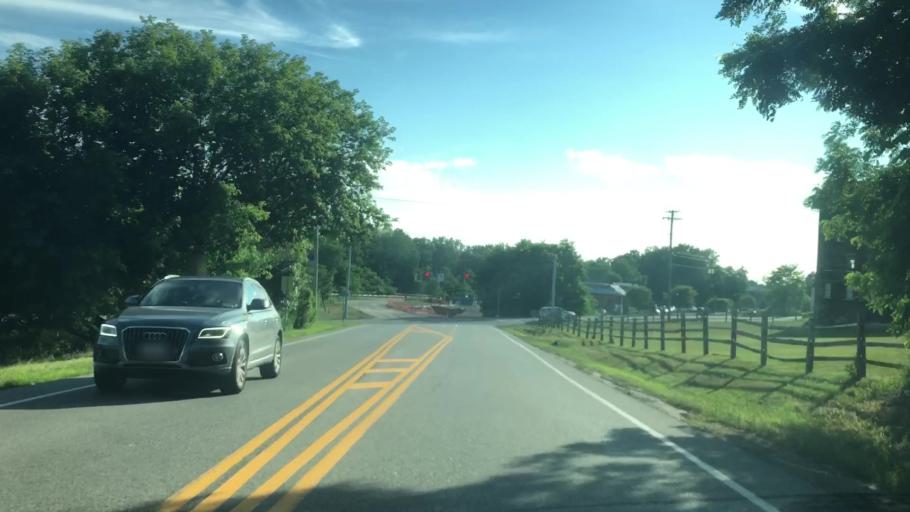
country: US
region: New York
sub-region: Ontario County
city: Victor
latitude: 43.0255
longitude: -77.4348
